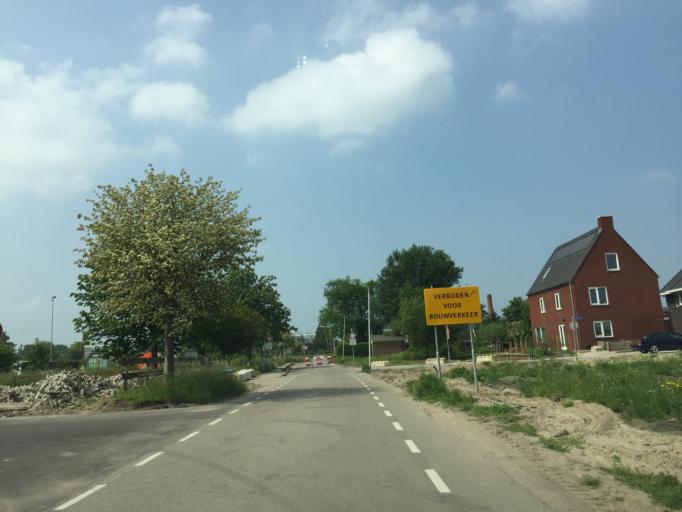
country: NL
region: South Holland
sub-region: Gemeente Pijnacker-Nootdorp
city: Pijnacker
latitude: 52.0183
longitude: 4.4416
